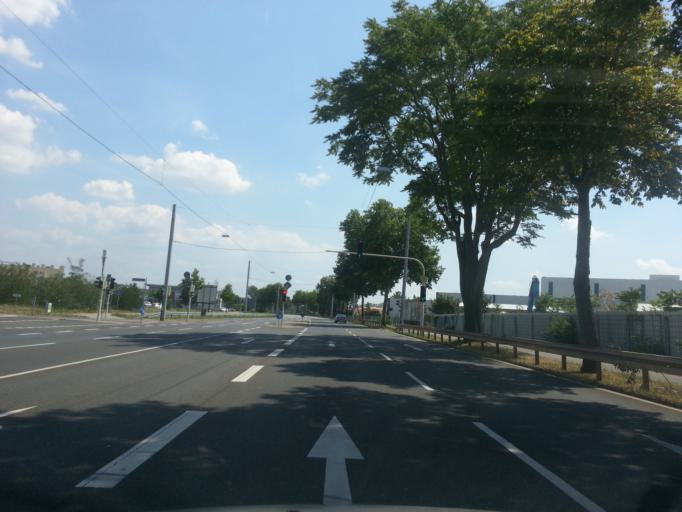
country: DE
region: Baden-Wuerttemberg
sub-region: Karlsruhe Region
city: Mannheim
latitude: 49.5405
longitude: 8.4645
